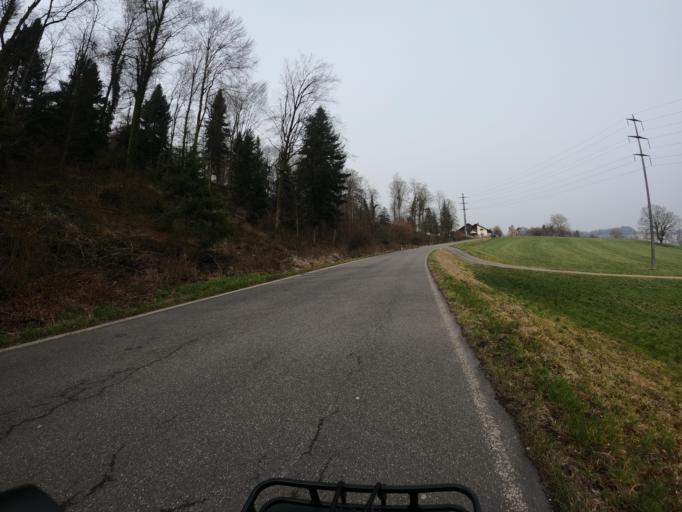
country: CH
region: Aargau
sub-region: Bezirk Baden
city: Mellingen
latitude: 47.4085
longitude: 8.2648
